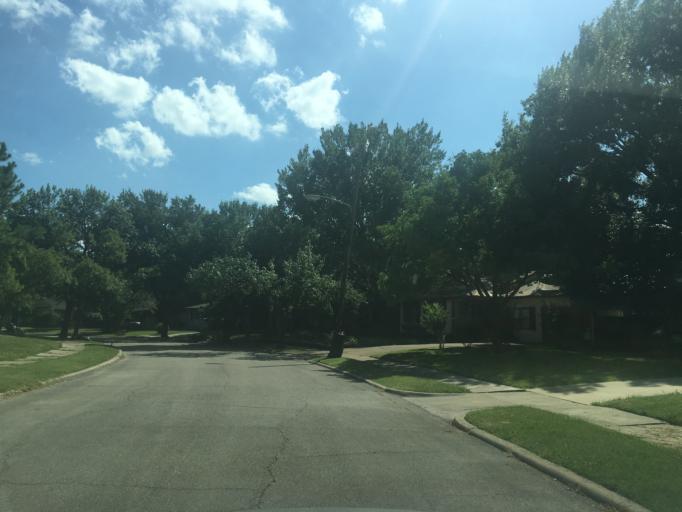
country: US
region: Texas
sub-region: Dallas County
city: Garland
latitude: 32.8343
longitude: -96.6865
